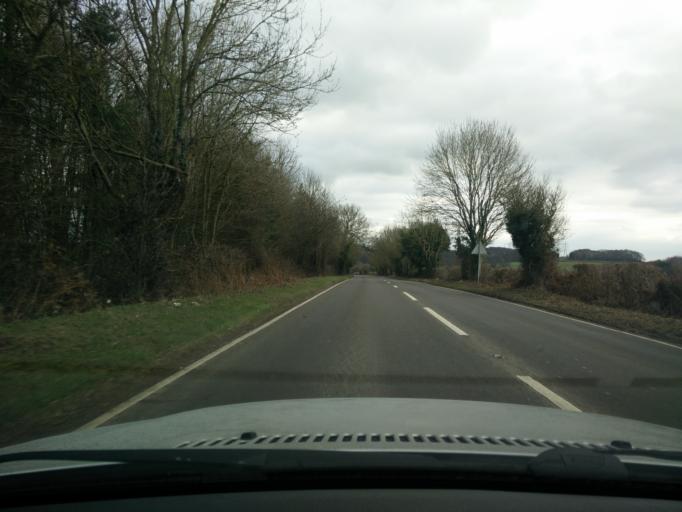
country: GB
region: England
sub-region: Buckinghamshire
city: Amersham
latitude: 51.6571
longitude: -0.6560
